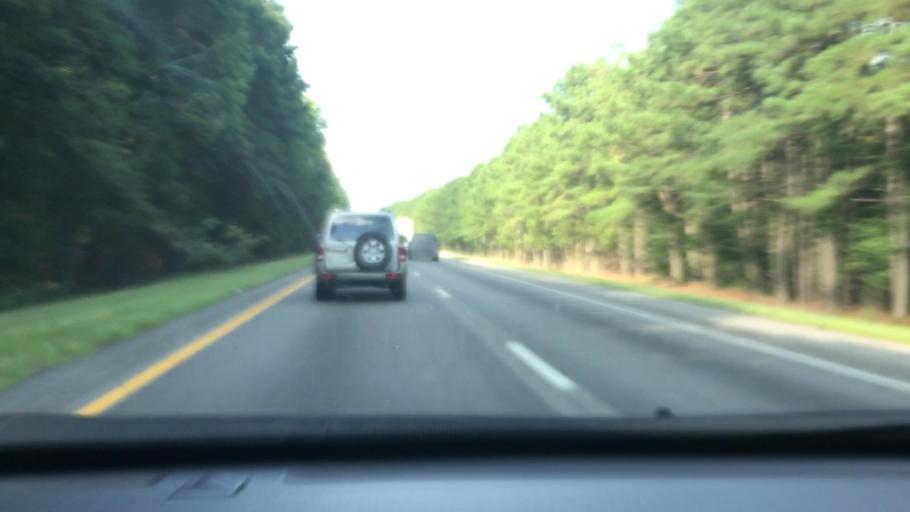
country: US
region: South Carolina
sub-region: Florence County
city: Timmonsville
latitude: 33.9900
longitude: -80.0190
